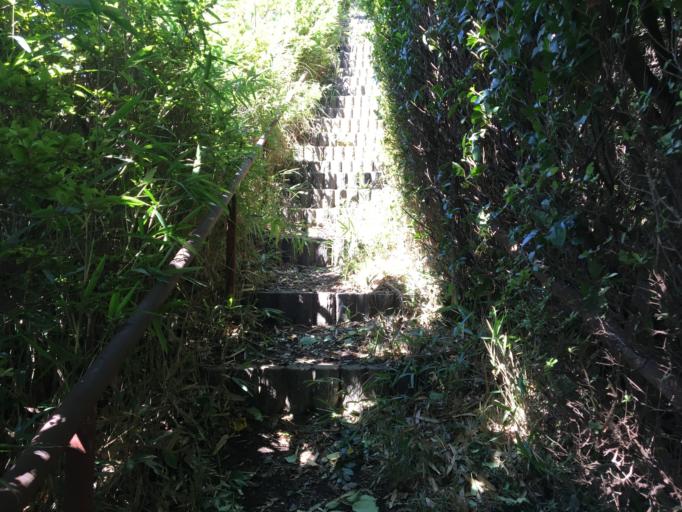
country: JP
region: Kanagawa
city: Yokohama
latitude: 35.5326
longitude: 139.5658
